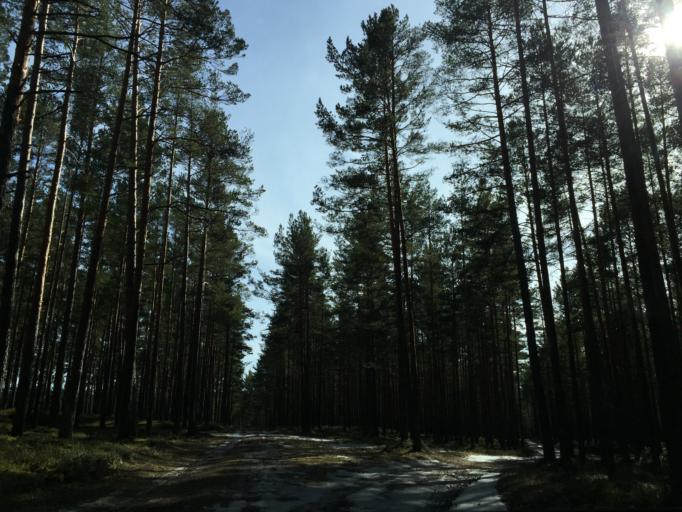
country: EE
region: Paernumaa
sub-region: Paernu linn
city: Parnu
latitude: 58.2342
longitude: 24.5185
